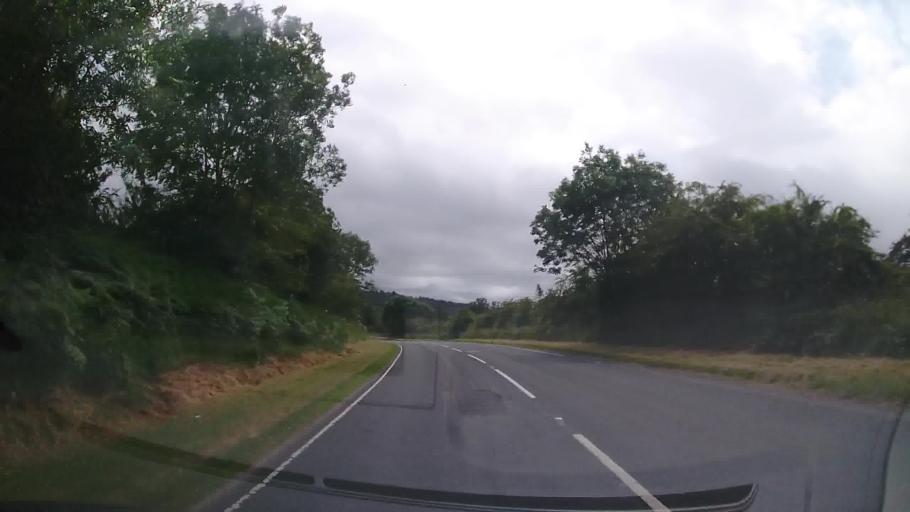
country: GB
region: Wales
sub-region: Denbighshire
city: Corwen
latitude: 52.9714
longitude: -3.3923
